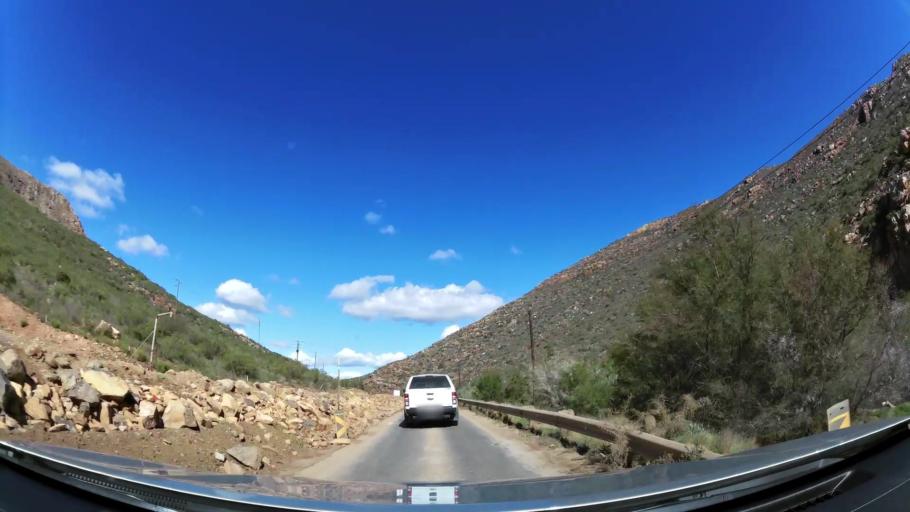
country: ZA
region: Western Cape
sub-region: Cape Winelands District Municipality
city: Ashton
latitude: -33.8142
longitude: 20.0902
